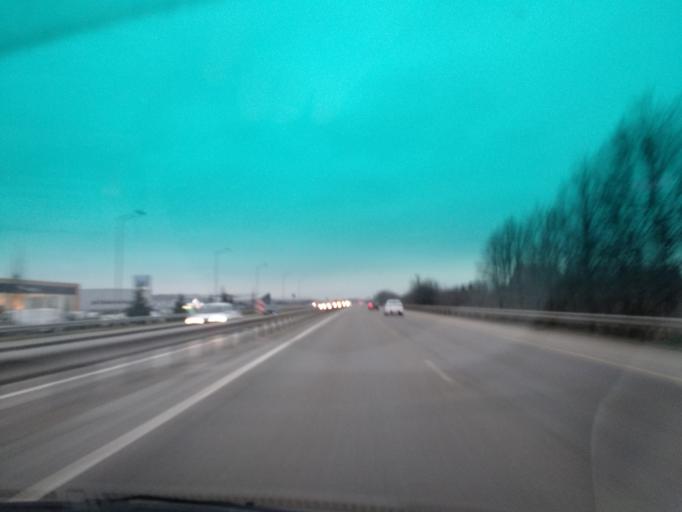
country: RU
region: Krasnodarskiy
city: Pashkovskiy
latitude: 45.0206
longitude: 39.1245
